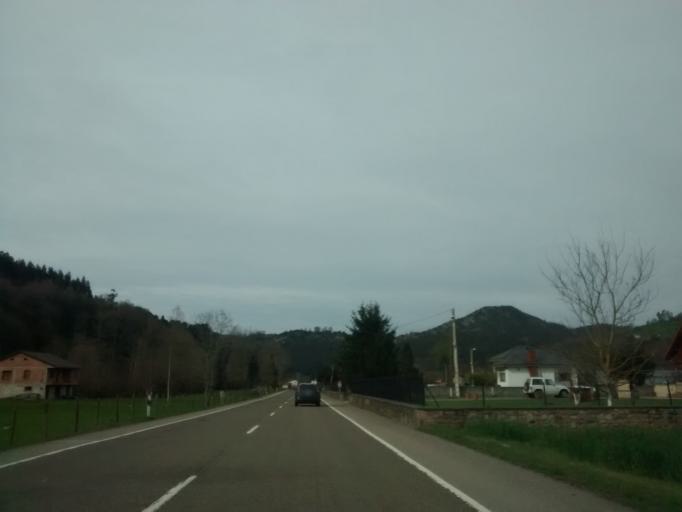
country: ES
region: Cantabria
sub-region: Provincia de Cantabria
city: Corvera
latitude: 43.2701
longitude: -3.9471
